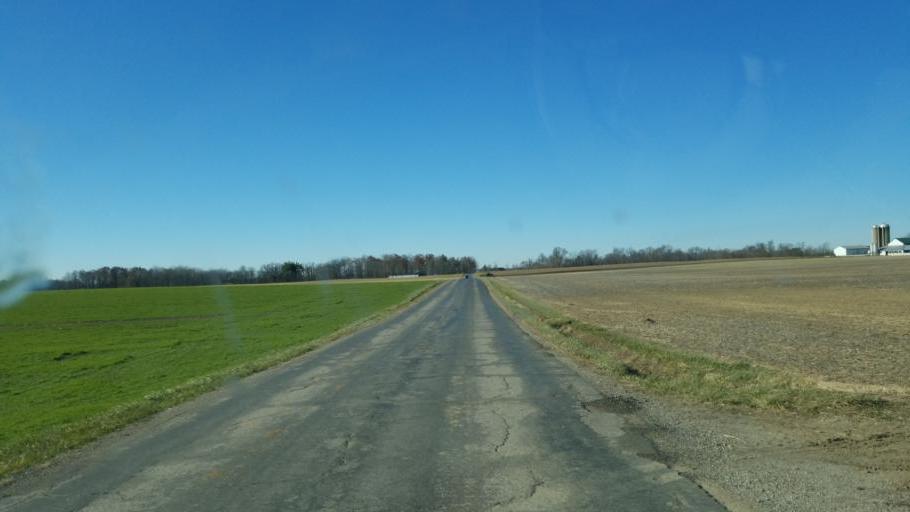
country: US
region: Ohio
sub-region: Huron County
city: Greenwich
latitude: 40.9603
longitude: -82.5626
